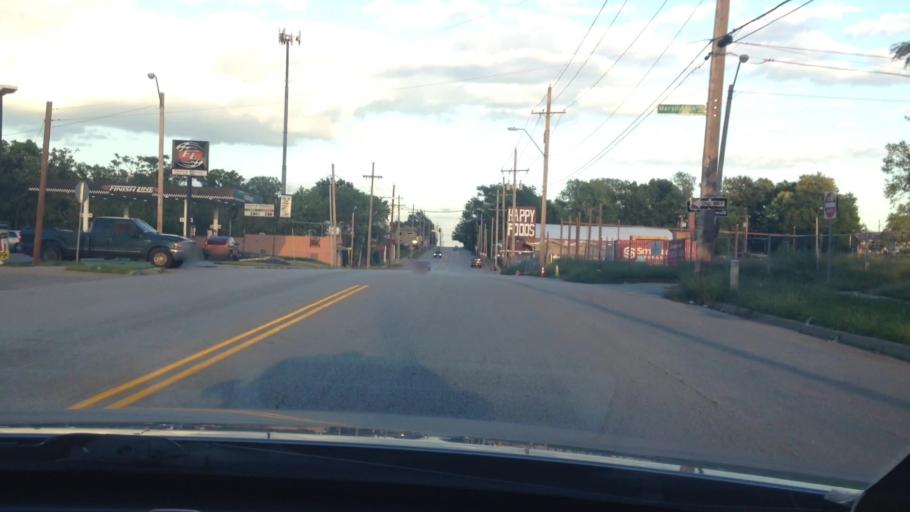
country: US
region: Missouri
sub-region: Jackson County
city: Kansas City
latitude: 39.0694
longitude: -94.5384
